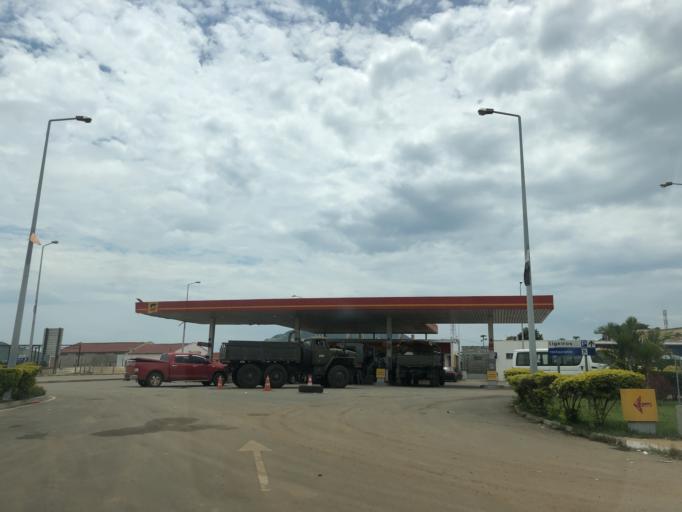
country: AO
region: Cuanza Sul
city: Quibala
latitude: -10.7315
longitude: 14.9795
